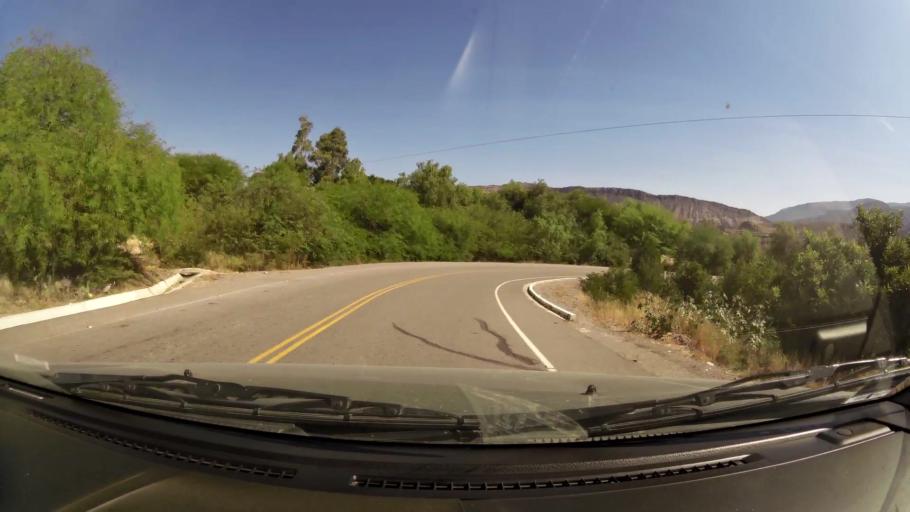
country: PE
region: Ayacucho
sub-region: Provincia de Huanta
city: Huanta
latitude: -12.9052
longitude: -74.3150
